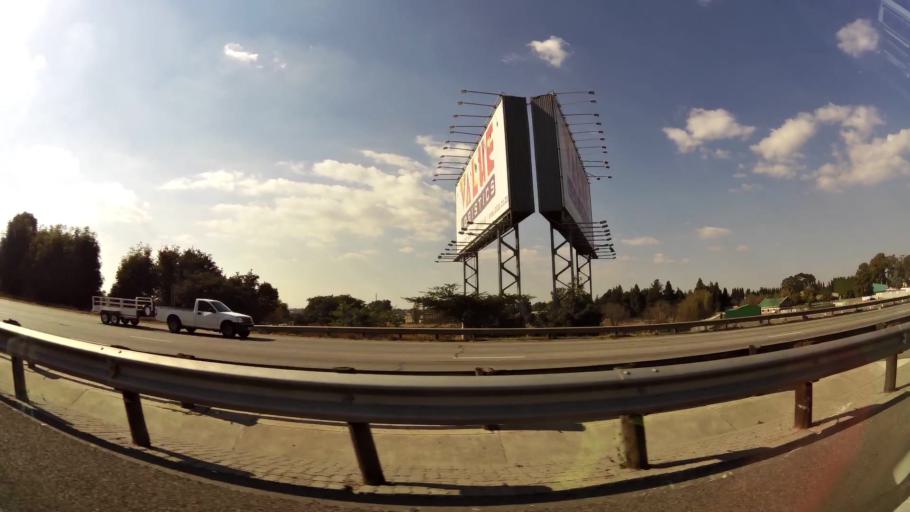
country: ZA
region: Gauteng
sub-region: Ekurhuleni Metropolitan Municipality
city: Tembisa
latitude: -26.0840
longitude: 28.2708
